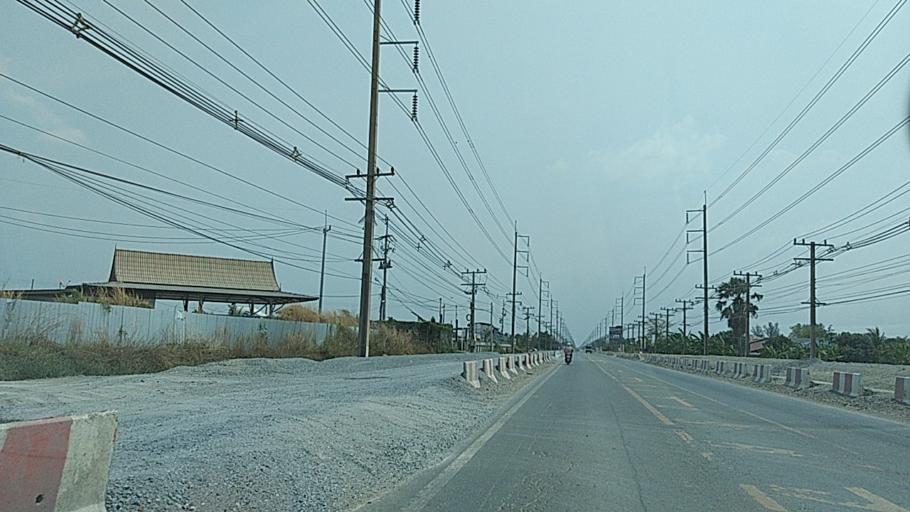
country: TH
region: Chon Buri
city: Phanat Nikhom
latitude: 13.4865
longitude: 101.1667
